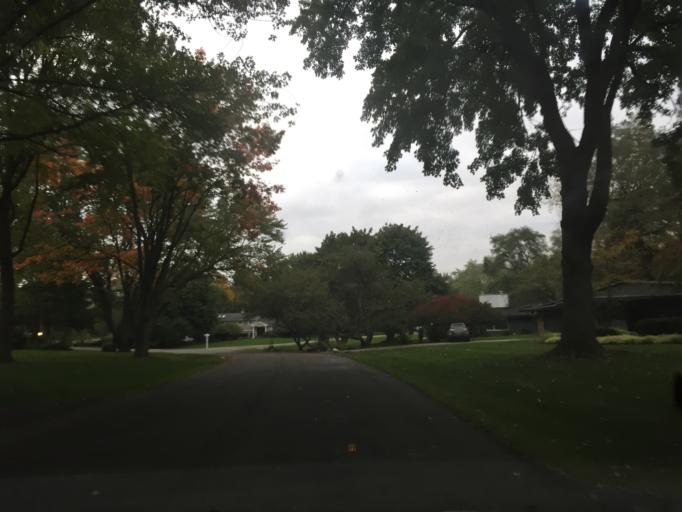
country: US
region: Michigan
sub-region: Oakland County
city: Franklin
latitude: 42.5573
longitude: -83.2886
